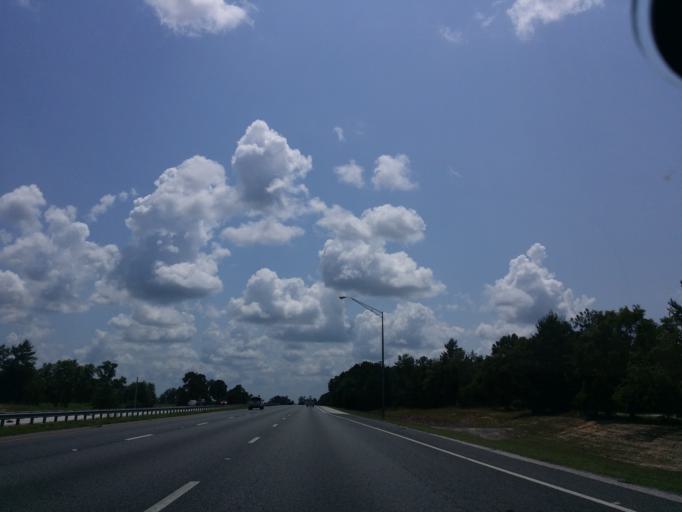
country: US
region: Florida
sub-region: Marion County
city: Ocala
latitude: 29.0882
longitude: -82.1852
